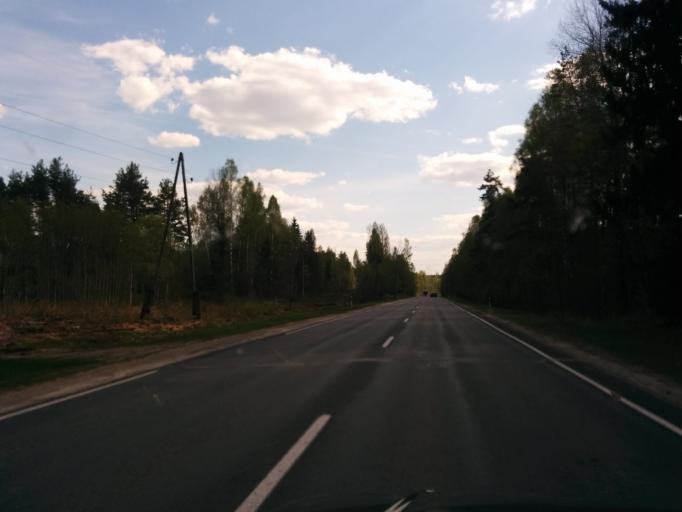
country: LV
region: Pargaujas
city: Stalbe
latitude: 57.3056
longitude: 24.9250
